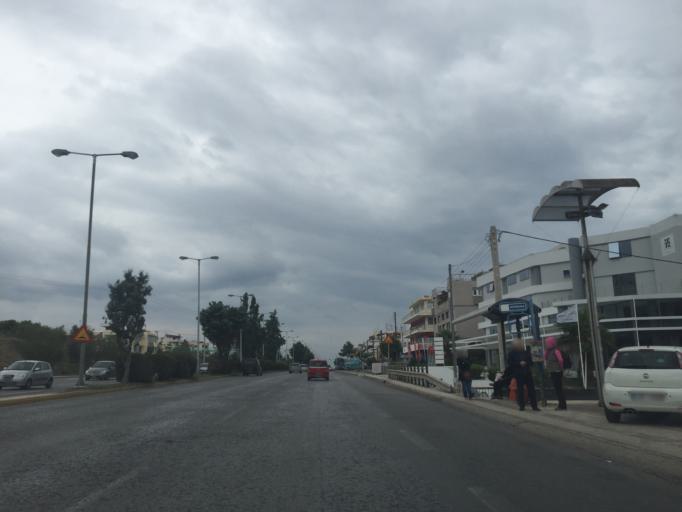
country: GR
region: Attica
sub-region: Nomarchia Athinas
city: Glyfada
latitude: 37.8533
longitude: 23.7670
